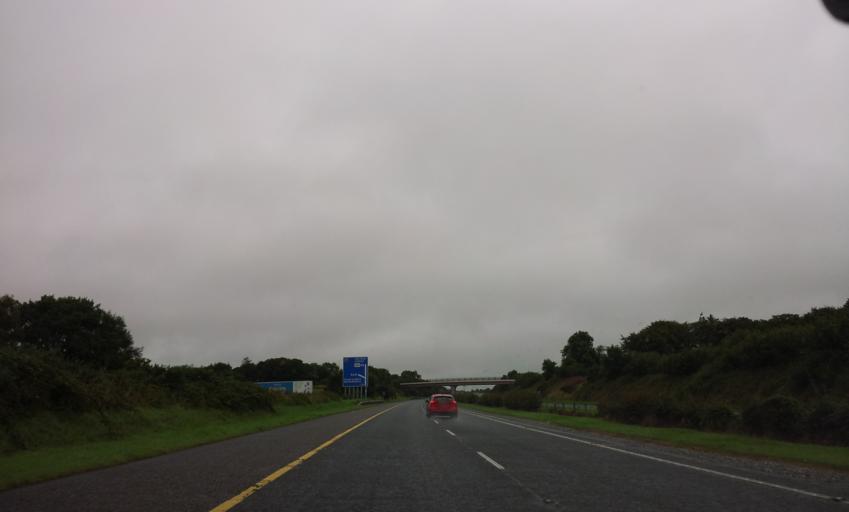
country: IE
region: Munster
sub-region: County Cork
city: Watergrasshill
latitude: 51.9938
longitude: -8.3574
